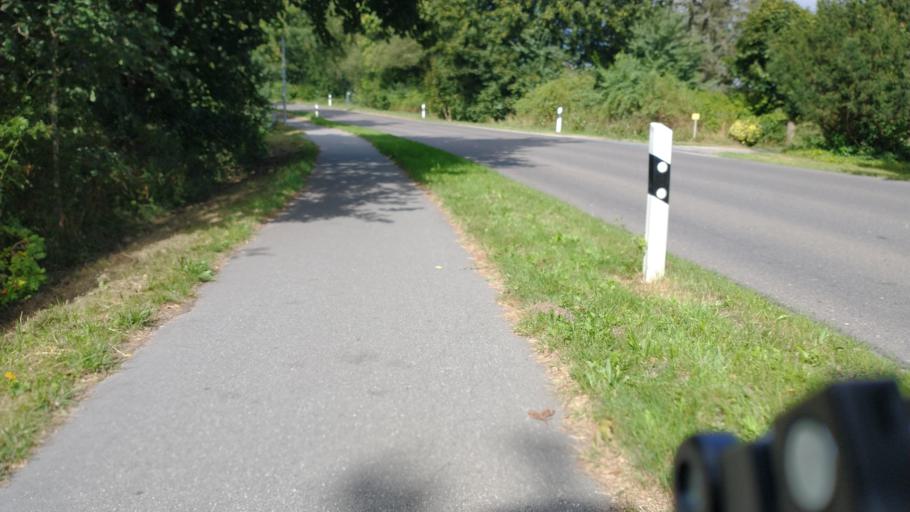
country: DE
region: Schleswig-Holstein
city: Bad Oldesloe
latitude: 53.8116
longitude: 10.3470
